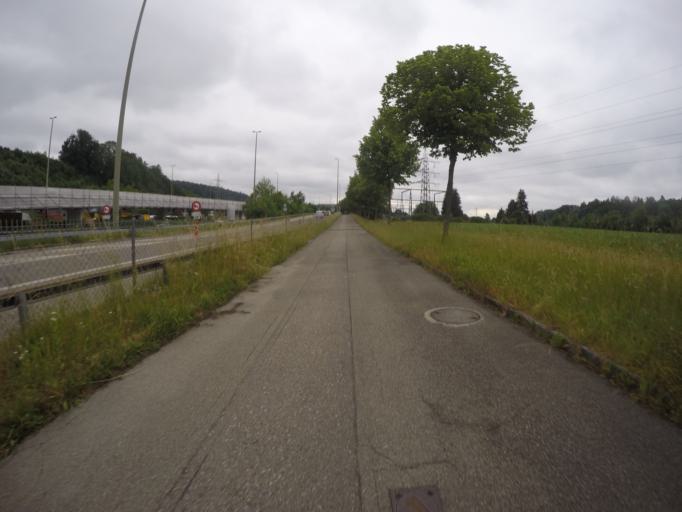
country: CH
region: Zurich
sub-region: Bezirk Winterthur
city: Toss
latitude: 47.4784
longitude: 8.7051
